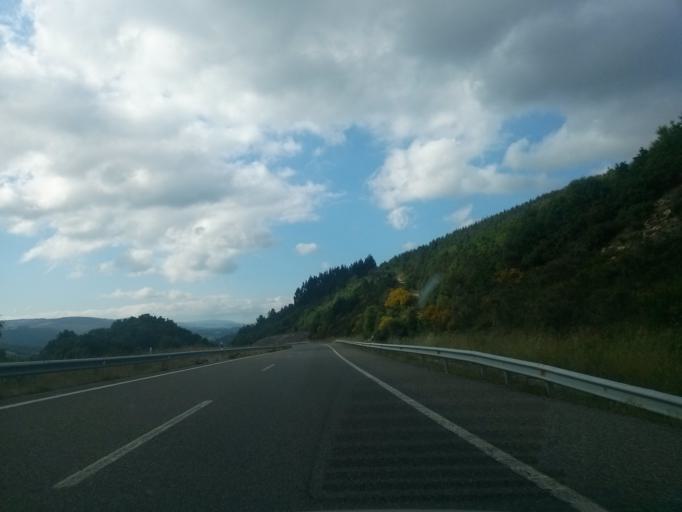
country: ES
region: Galicia
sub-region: Provincia de Lugo
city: Becerrea
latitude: 42.8918
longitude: -7.1837
